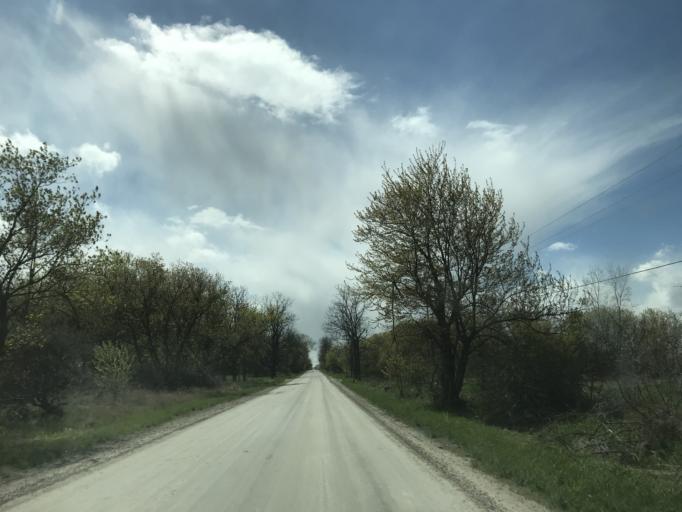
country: US
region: Michigan
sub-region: Oakland County
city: South Lyon
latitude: 42.3884
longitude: -83.6295
